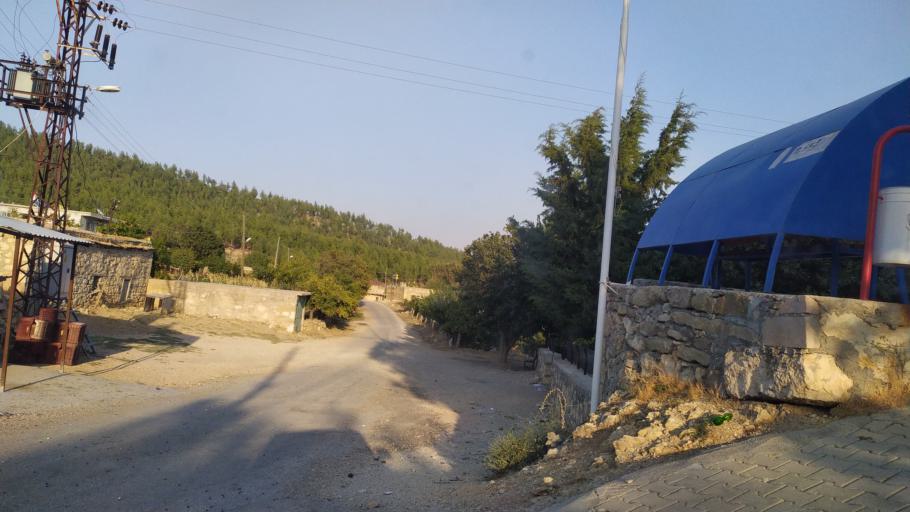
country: TR
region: Mersin
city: Mut
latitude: 36.6929
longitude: 33.2006
